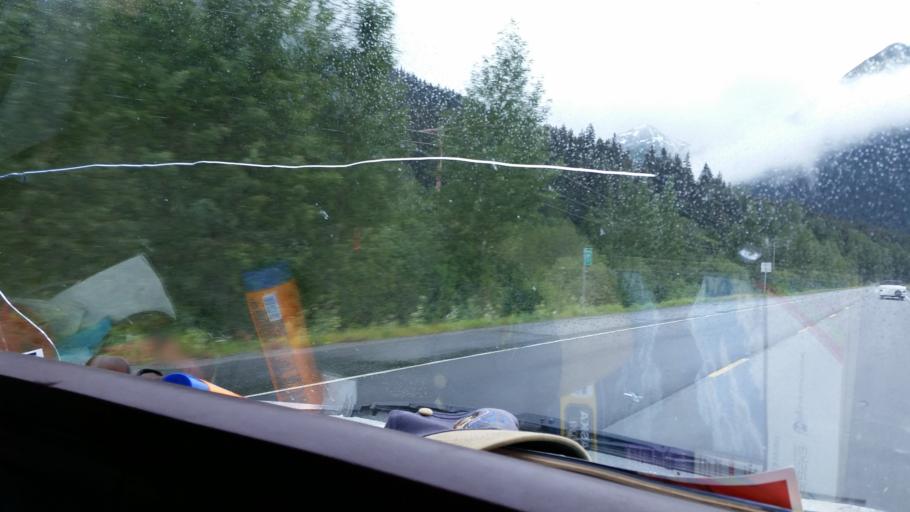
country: US
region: Alaska
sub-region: Anchorage Municipality
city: Girdwood
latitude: 60.9150
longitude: -149.1063
